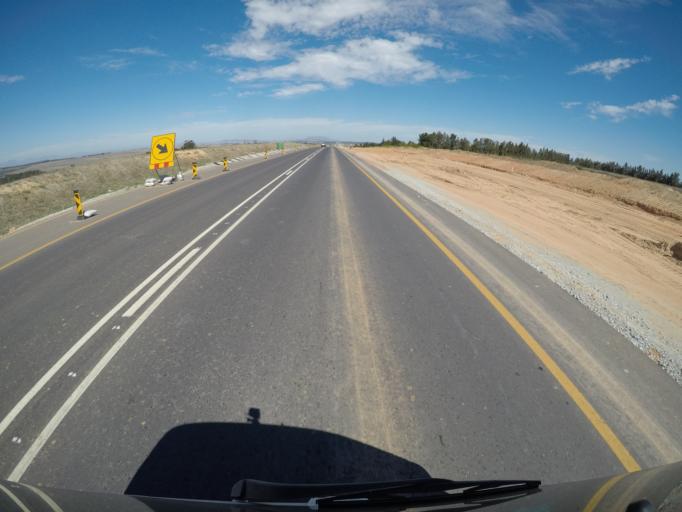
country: ZA
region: Western Cape
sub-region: West Coast District Municipality
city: Malmesbury
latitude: -33.5007
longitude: 18.6640
